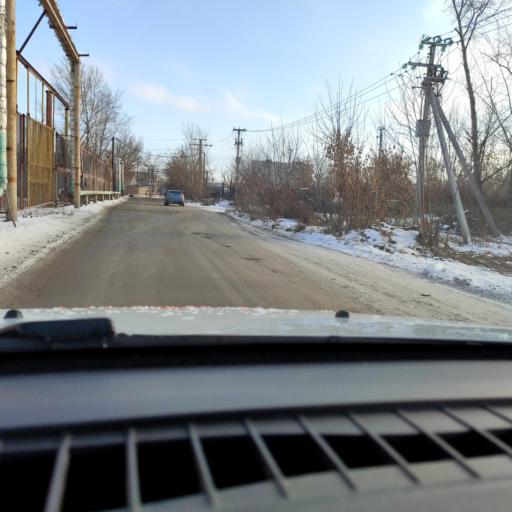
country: RU
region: Samara
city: Tol'yatti
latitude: 53.5316
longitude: 49.2576
